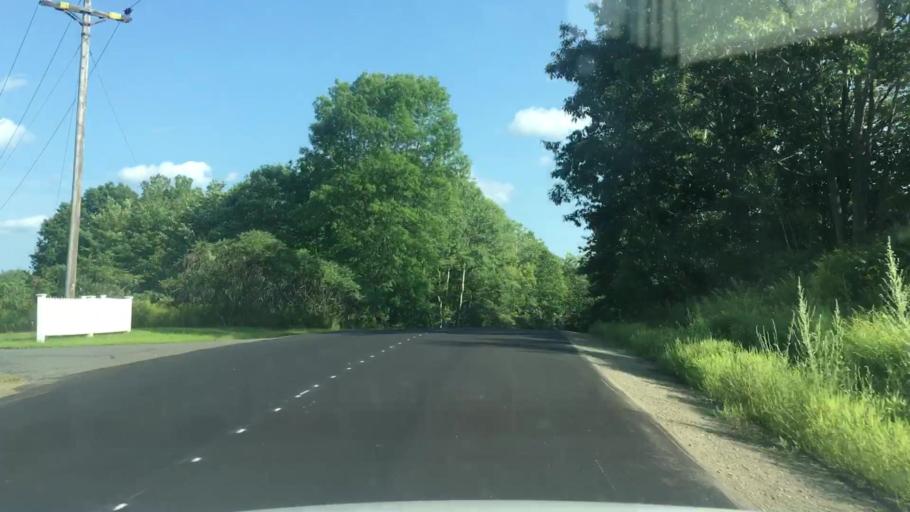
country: US
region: Maine
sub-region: Kennebec County
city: Waterville
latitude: 44.5760
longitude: -69.6599
